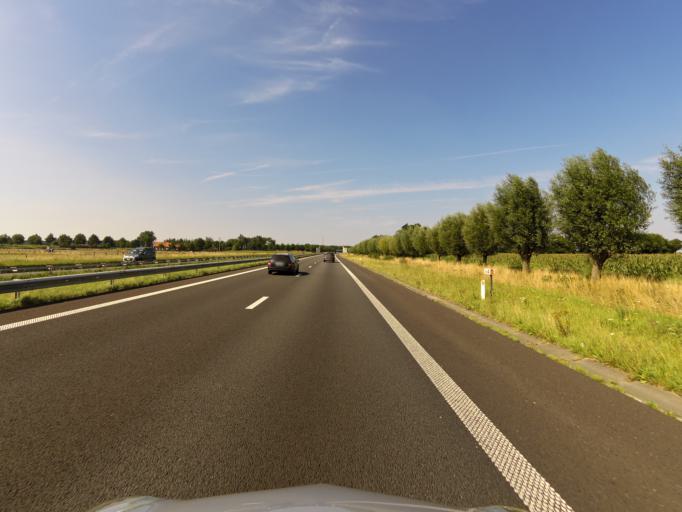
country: BE
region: Flanders
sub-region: Provincie West-Vlaanderen
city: Lichtervelde
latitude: 51.0596
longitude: 3.1581
